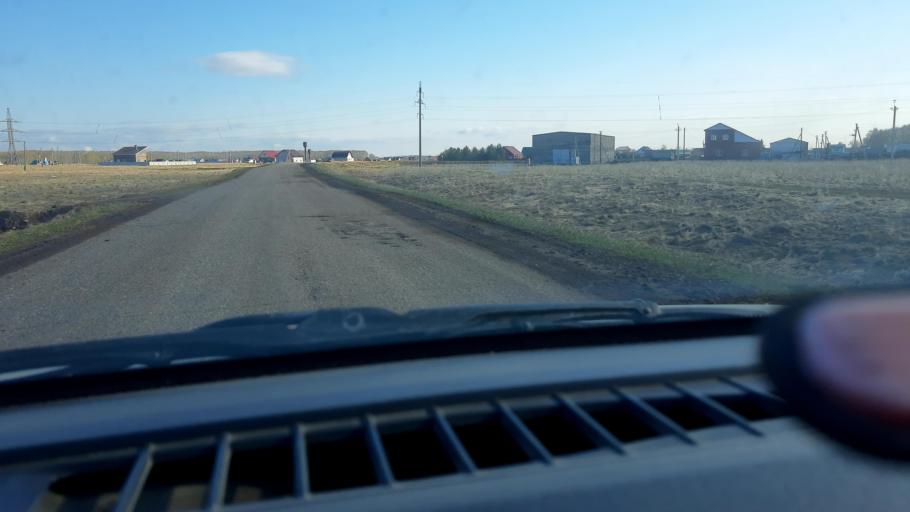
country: RU
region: Bashkortostan
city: Asanovo
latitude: 54.9570
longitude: 55.5347
